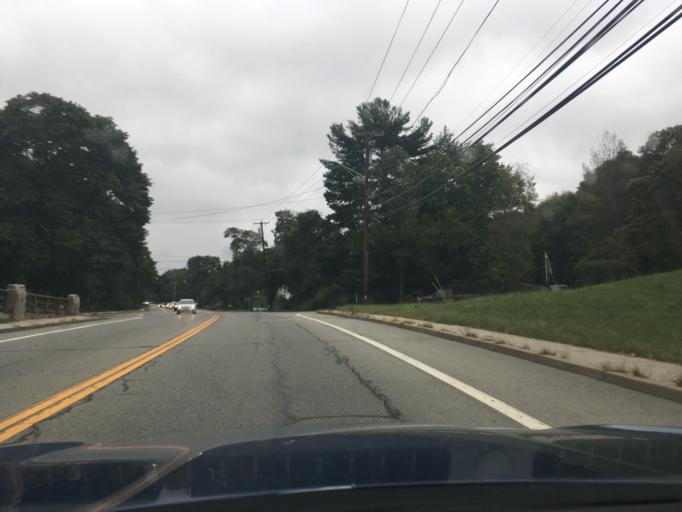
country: US
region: Rhode Island
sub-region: Washington County
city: North Kingstown
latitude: 41.5790
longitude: -71.4919
